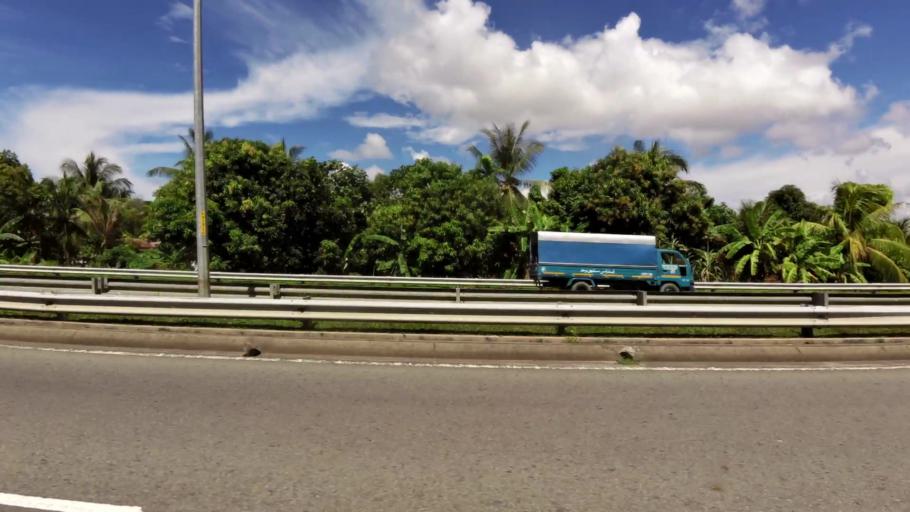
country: BN
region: Brunei and Muara
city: Bandar Seri Begawan
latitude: 4.9677
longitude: 114.9525
